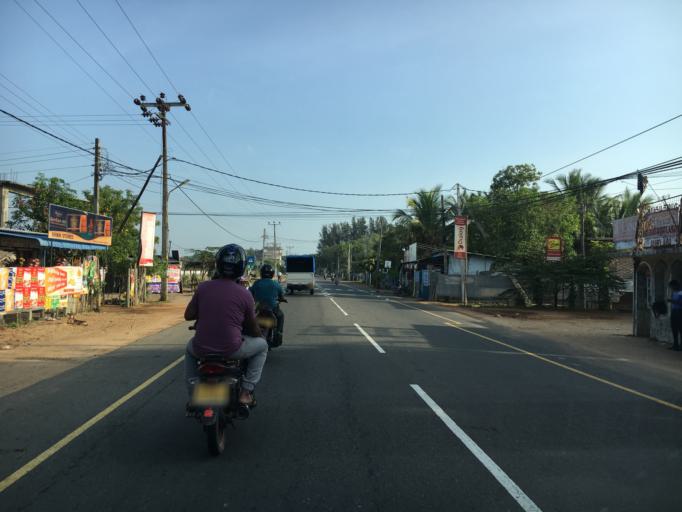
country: LK
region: Eastern Province
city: Eravur Town
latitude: 7.9023
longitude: 81.5351
